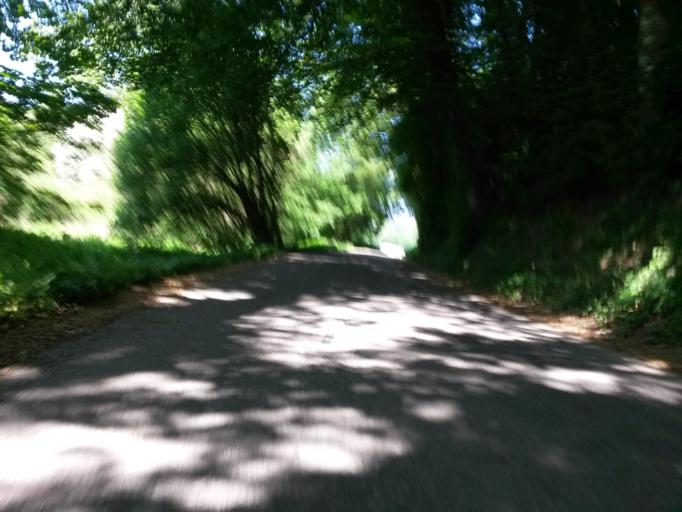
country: CH
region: Bern
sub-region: Bern-Mittelland District
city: Muhleberg
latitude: 46.9728
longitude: 7.2518
